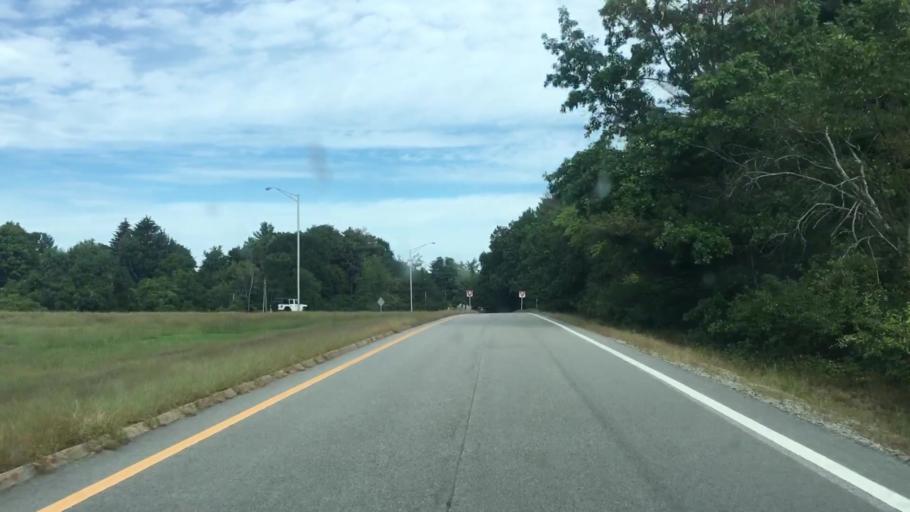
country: US
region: New Hampshire
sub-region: Strafford County
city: Dover
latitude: 43.1856
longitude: -70.8850
